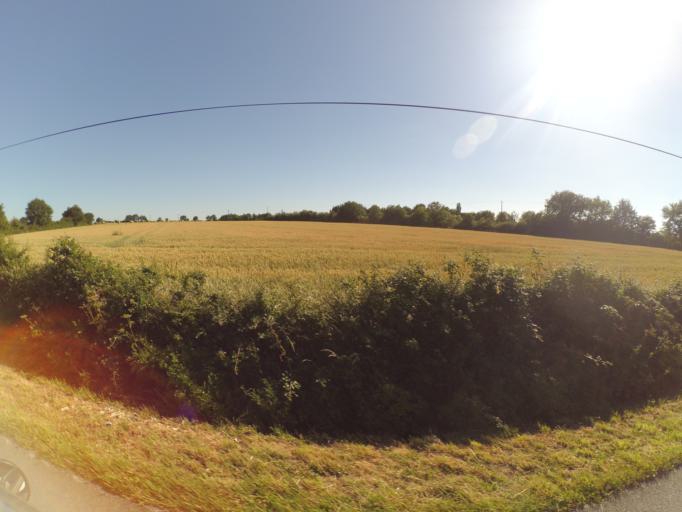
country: FR
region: Pays de la Loire
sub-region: Departement de la Vendee
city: La Boissiere-de-Montaigu
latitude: 46.9148
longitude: -1.1511
